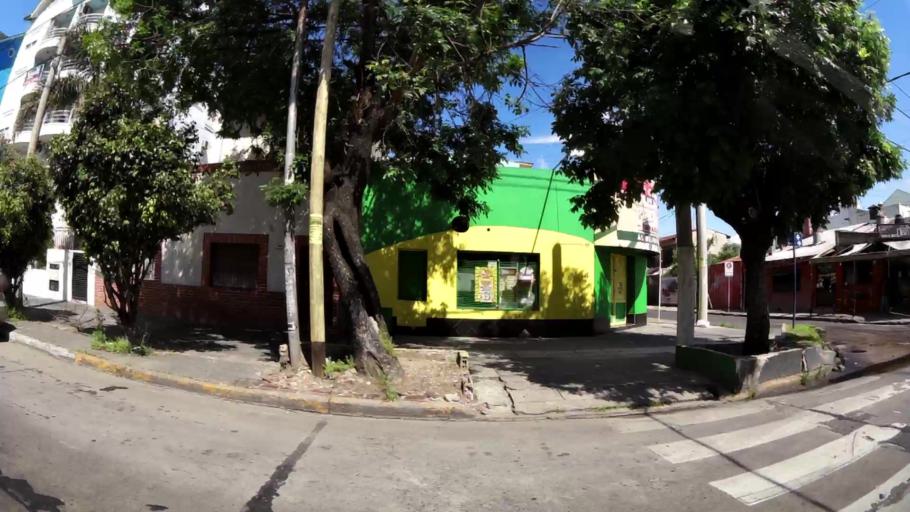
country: AR
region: Buenos Aires
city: San Justo
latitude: -34.6723
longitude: -58.5602
